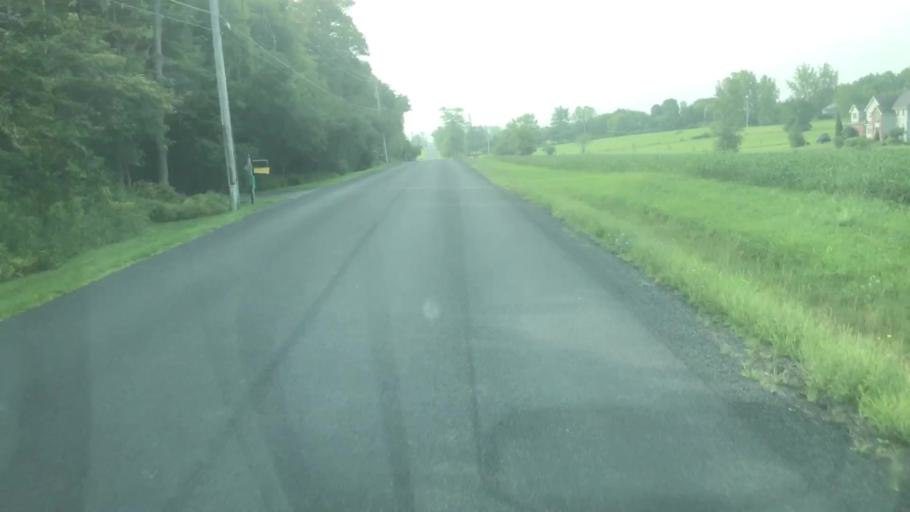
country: US
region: New York
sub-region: Onondaga County
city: Skaneateles
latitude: 42.9342
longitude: -76.4578
